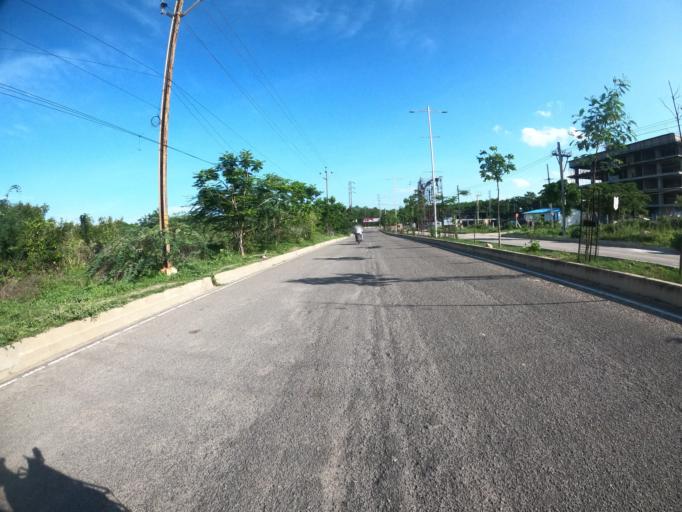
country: IN
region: Telangana
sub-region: Hyderabad
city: Hyderabad
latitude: 17.3518
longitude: 78.3698
